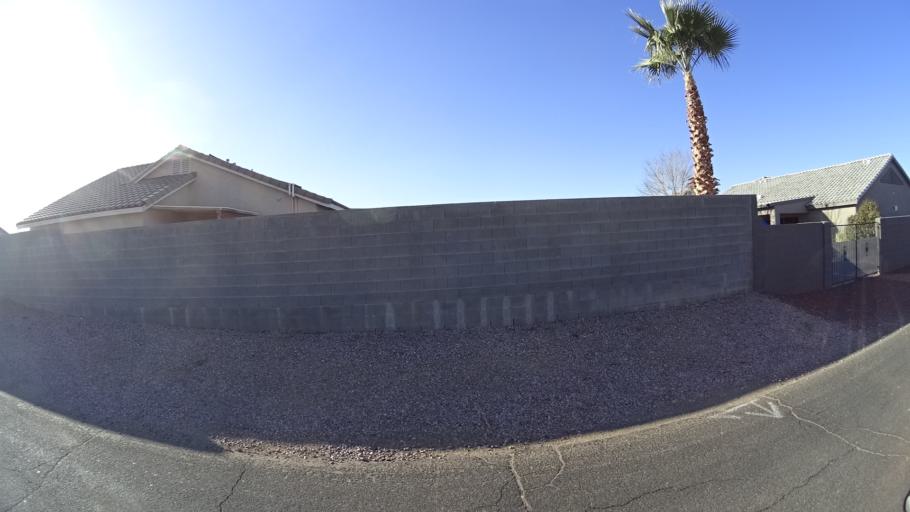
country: US
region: Arizona
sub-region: Mohave County
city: Kingman
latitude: 35.2140
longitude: -114.0079
